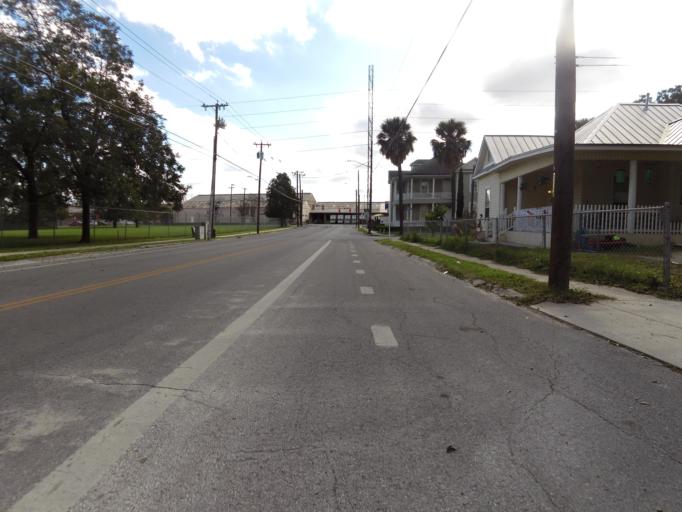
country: US
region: Texas
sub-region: Bexar County
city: San Antonio
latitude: 29.4114
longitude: -98.4982
